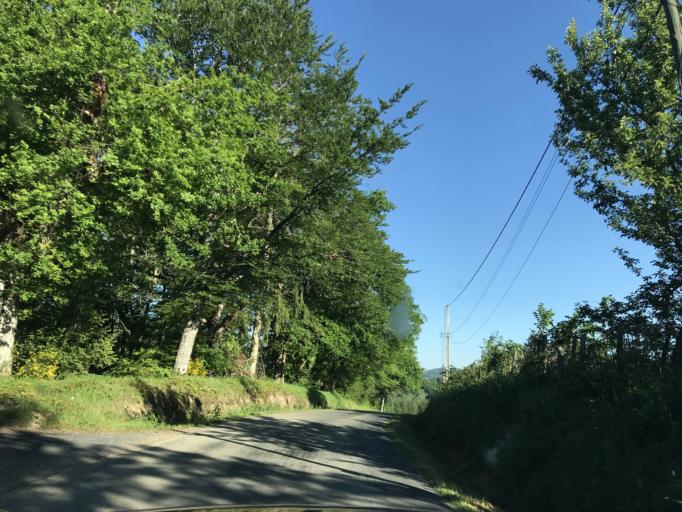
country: FR
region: Auvergne
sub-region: Departement du Puy-de-Dome
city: Job
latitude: 45.6567
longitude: 3.6641
